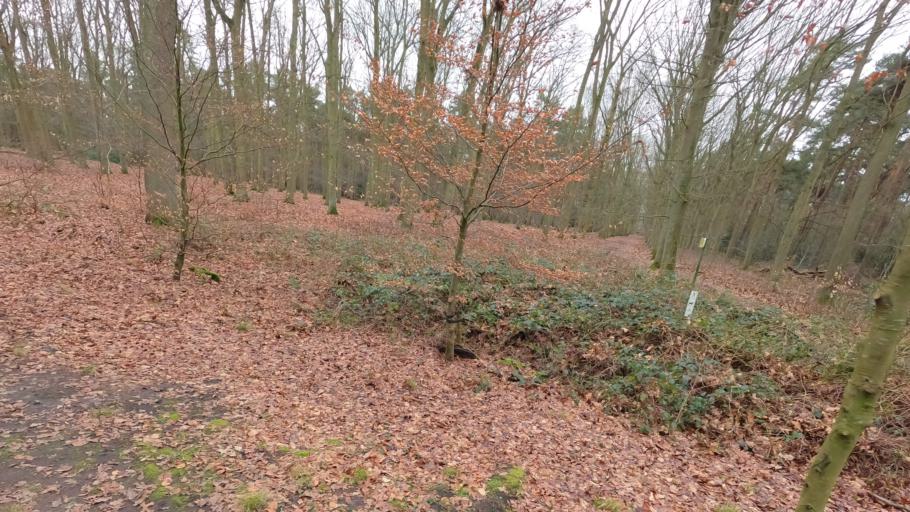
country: BE
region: Flanders
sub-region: Provincie Antwerpen
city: Brasschaat
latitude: 51.2820
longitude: 4.4859
